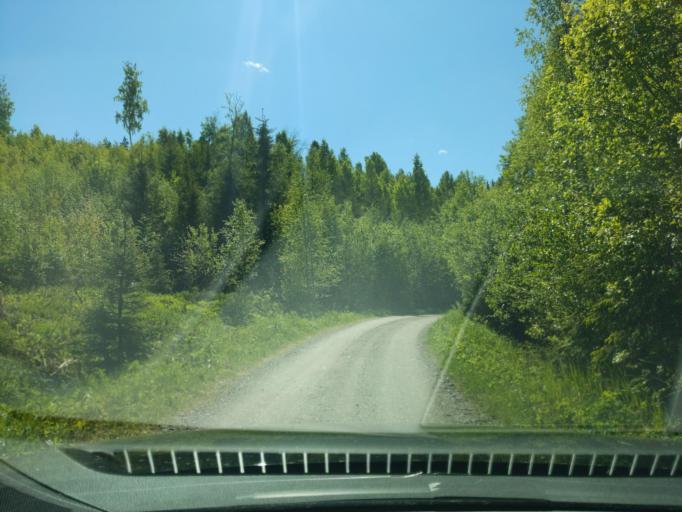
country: FI
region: Paijanne Tavastia
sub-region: Lahti
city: Lahti
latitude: 61.0591
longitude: 25.7013
